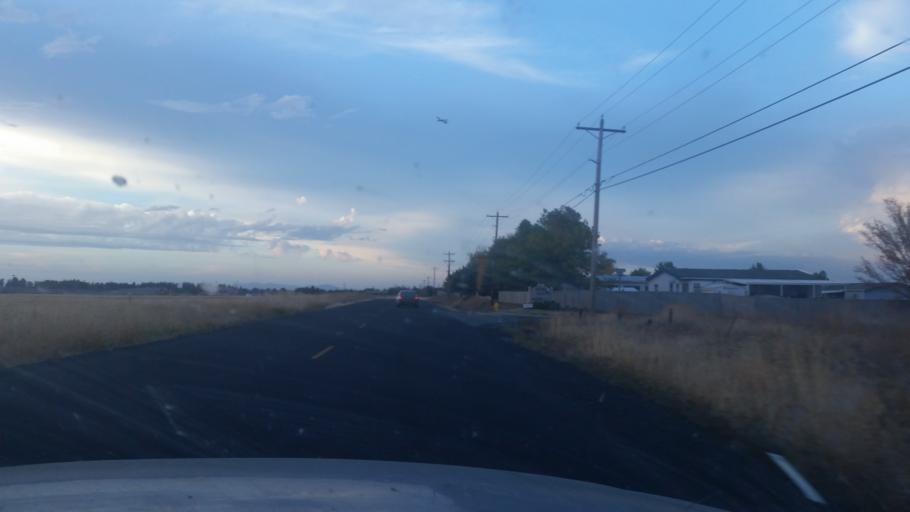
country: US
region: Washington
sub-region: Spokane County
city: Airway Heights
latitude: 47.5815
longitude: -117.5645
